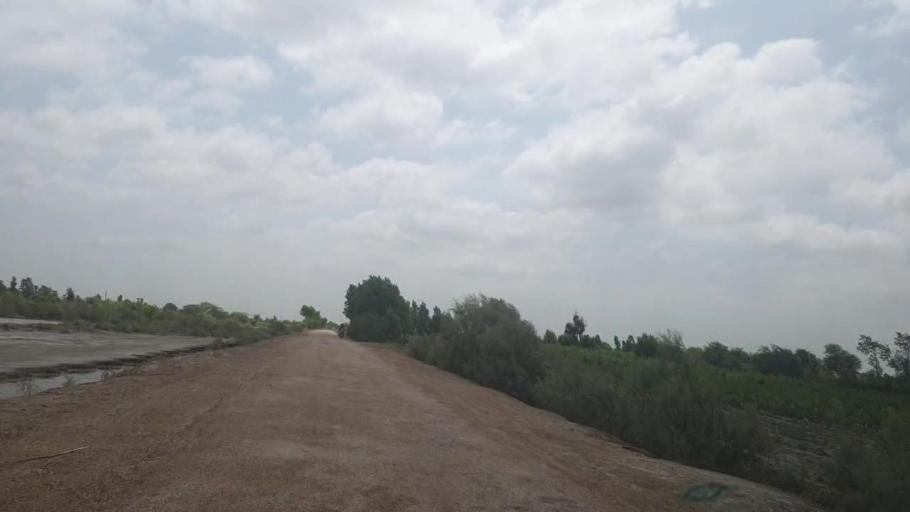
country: PK
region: Sindh
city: Tando Mittha Khan
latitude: 25.8867
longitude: 69.1357
